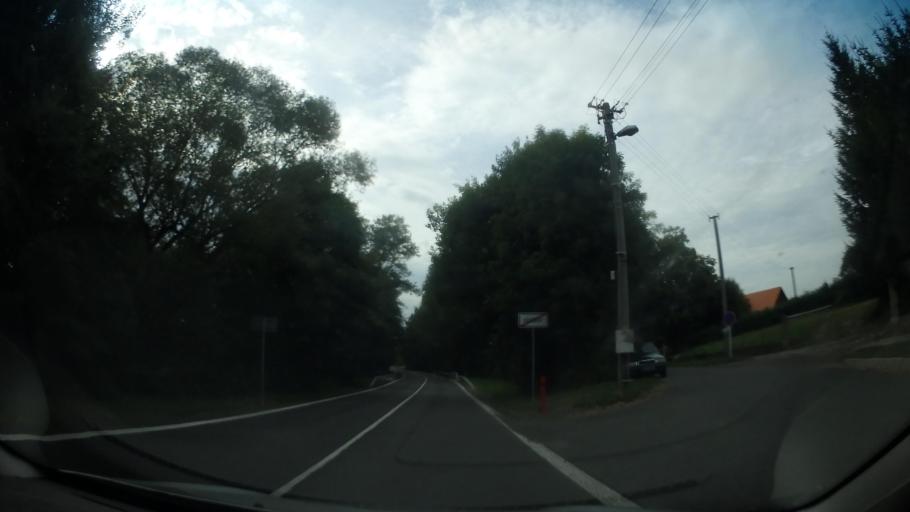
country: CZ
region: Pardubicky
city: Prachovice
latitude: 49.8692
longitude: 15.6242
